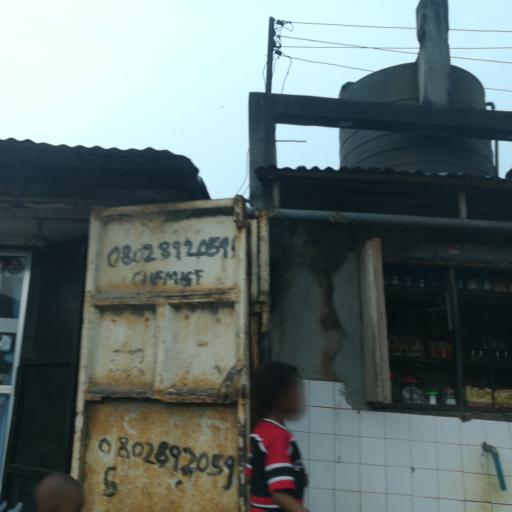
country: NG
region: Rivers
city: Port Harcourt
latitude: 4.7545
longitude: 7.0104
